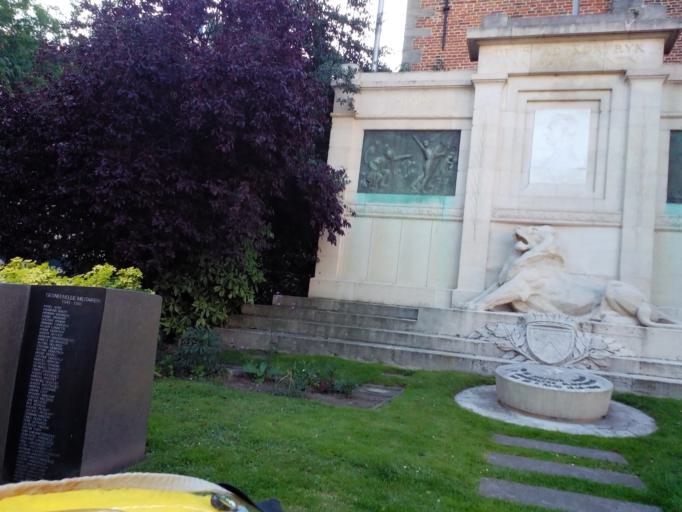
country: BE
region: Flanders
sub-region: Provincie West-Vlaanderen
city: Kortrijk
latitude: 50.8275
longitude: 3.2658
